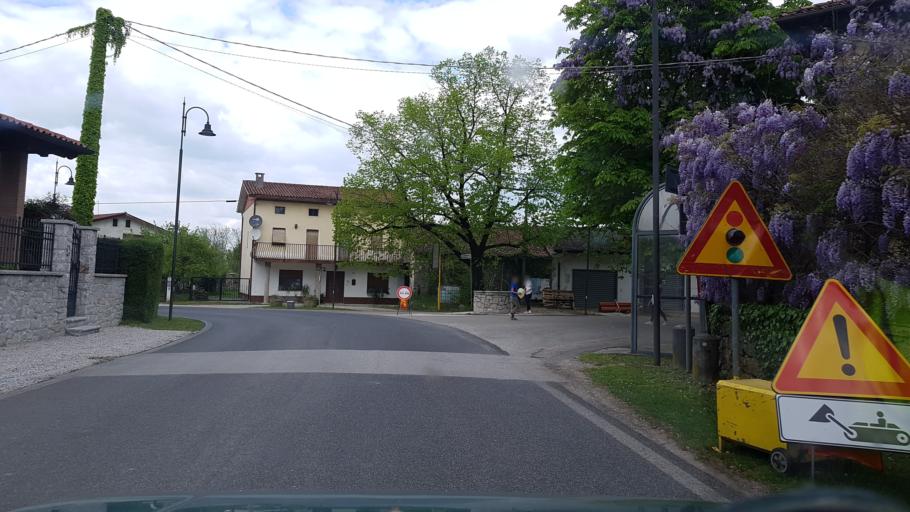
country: IT
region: Friuli Venezia Giulia
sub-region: Provincia di Gorizia
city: Savogna d'Isonzo
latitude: 45.8866
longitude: 13.5816
